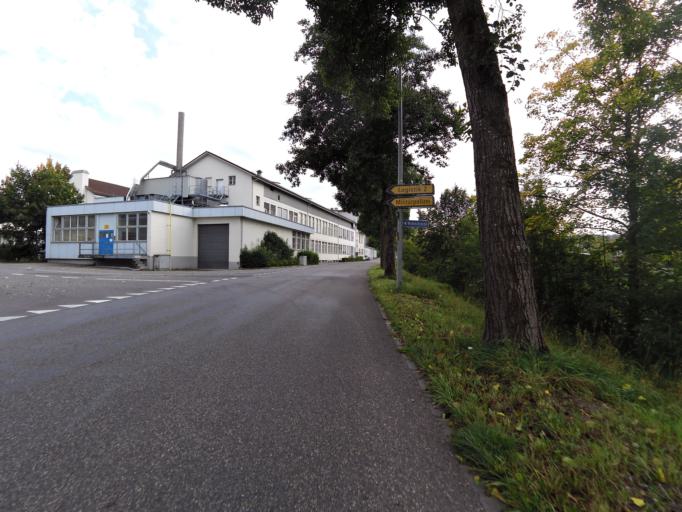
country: CH
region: Thurgau
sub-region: Frauenfeld District
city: Frauenfeld
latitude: 47.5623
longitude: 8.8982
